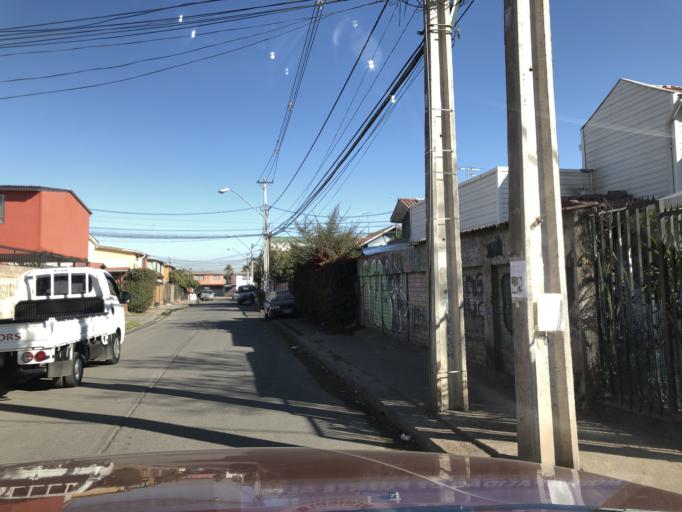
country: CL
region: Santiago Metropolitan
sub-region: Provincia de Cordillera
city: Puente Alto
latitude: -33.5936
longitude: -70.5627
